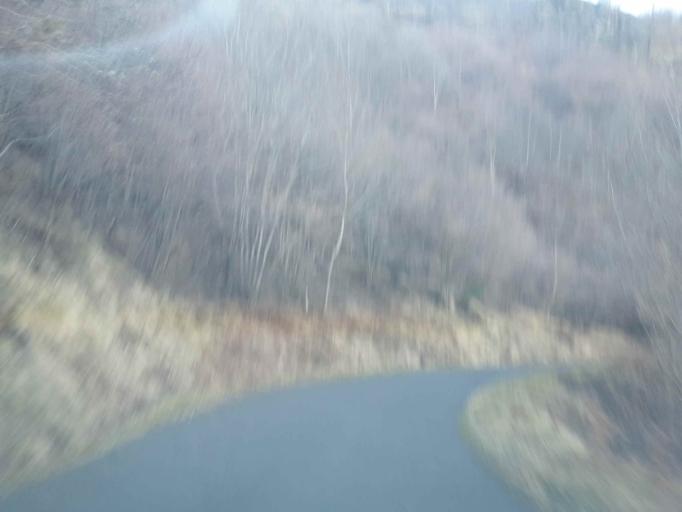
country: FR
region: Auvergne
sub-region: Departement du Cantal
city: Riom-es-Montagnes
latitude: 45.1662
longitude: 2.6074
